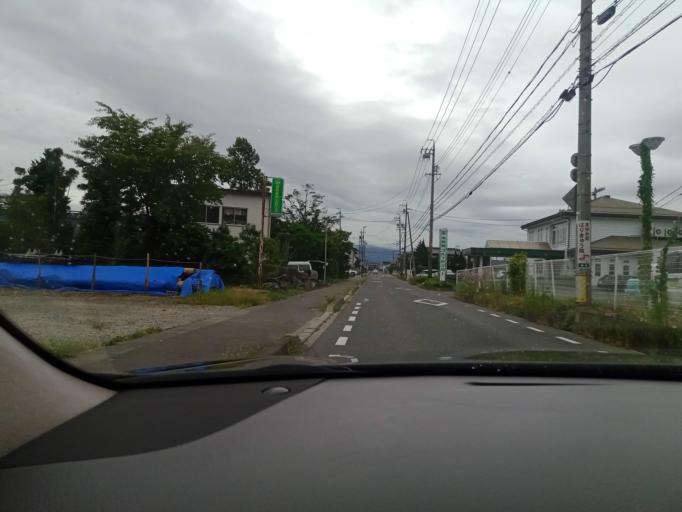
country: JP
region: Nagano
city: Nagano-shi
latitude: 36.6797
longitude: 138.2078
